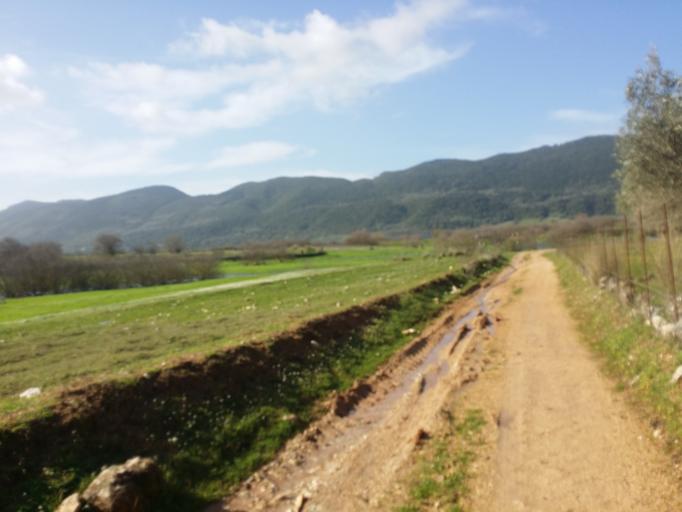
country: GR
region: West Greece
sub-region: Nomos Aitolias kai Akarnanias
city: Fitiai
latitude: 38.7440
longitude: 21.1972
